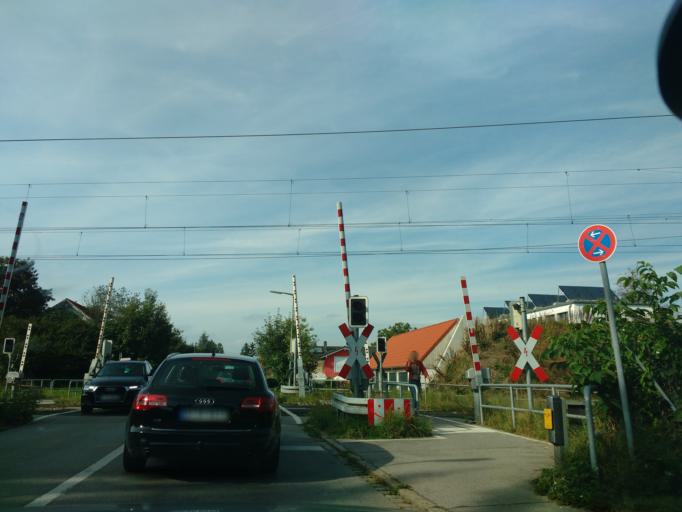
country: DE
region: Bavaria
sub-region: Upper Bavaria
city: Pasing
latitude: 48.1537
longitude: 11.4357
